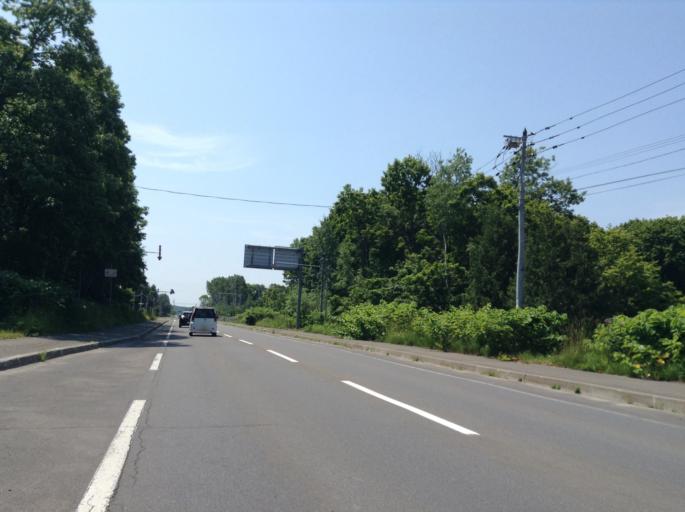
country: JP
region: Hokkaido
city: Nayoro
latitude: 44.3455
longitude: 142.4749
